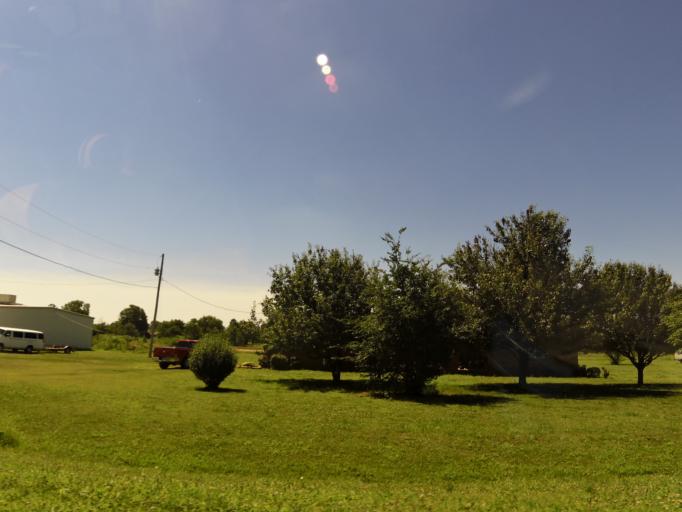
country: US
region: Missouri
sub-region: New Madrid County
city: Lilbourn
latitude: 36.5688
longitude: -89.5951
